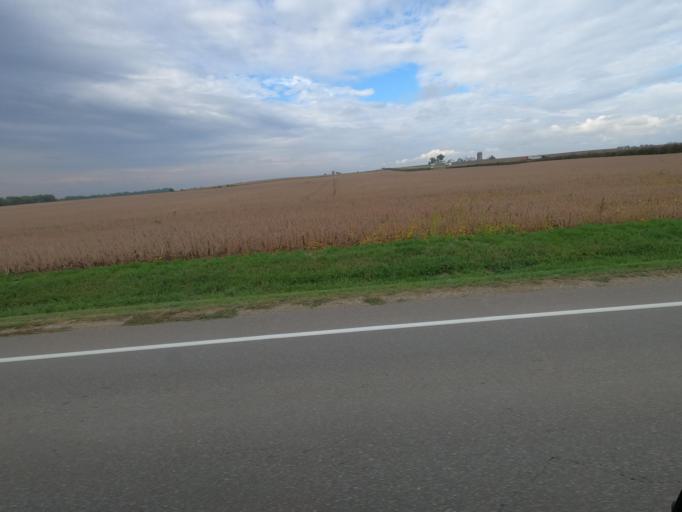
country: US
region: Iowa
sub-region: Henry County
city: Mount Pleasant
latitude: 40.7845
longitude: -91.5664
